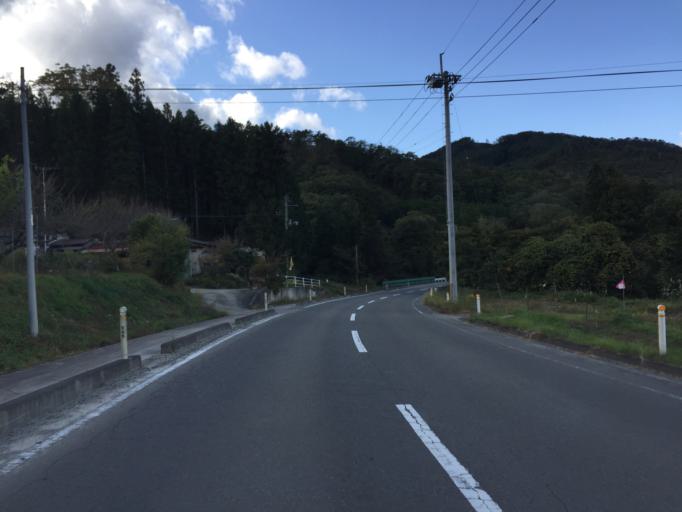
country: JP
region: Miyagi
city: Marumori
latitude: 37.8379
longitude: 140.8305
